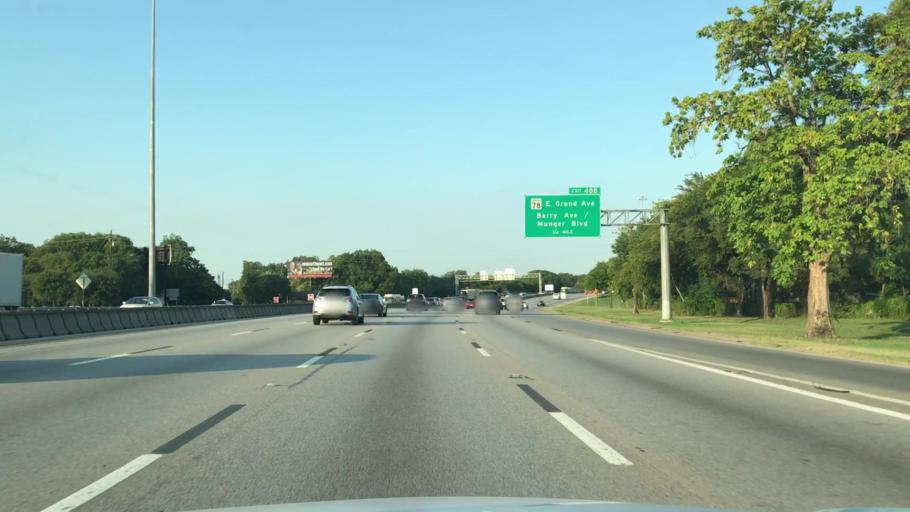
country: US
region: Texas
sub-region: Dallas County
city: Dallas
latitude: 32.7902
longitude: -96.7631
